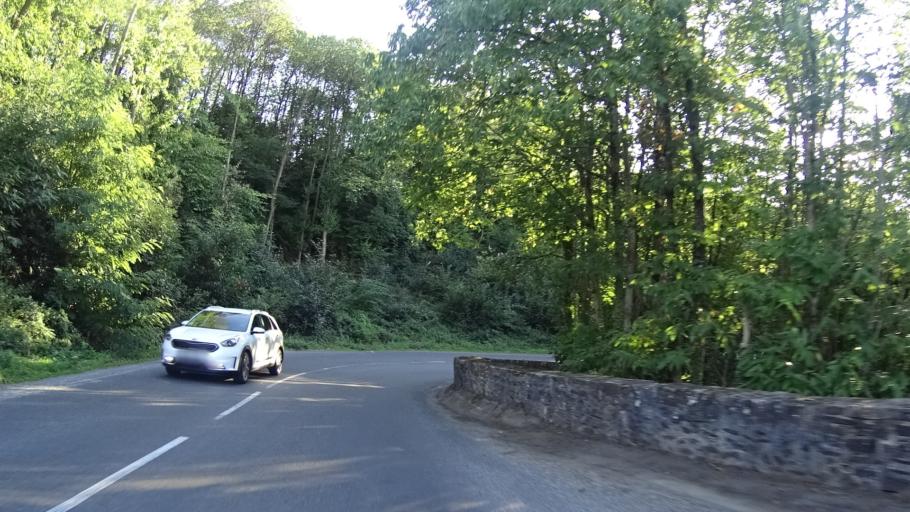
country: FR
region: Pays de la Loire
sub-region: Departement de Maine-et-Loire
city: Champtoceaux
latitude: 47.3391
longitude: -1.2672
